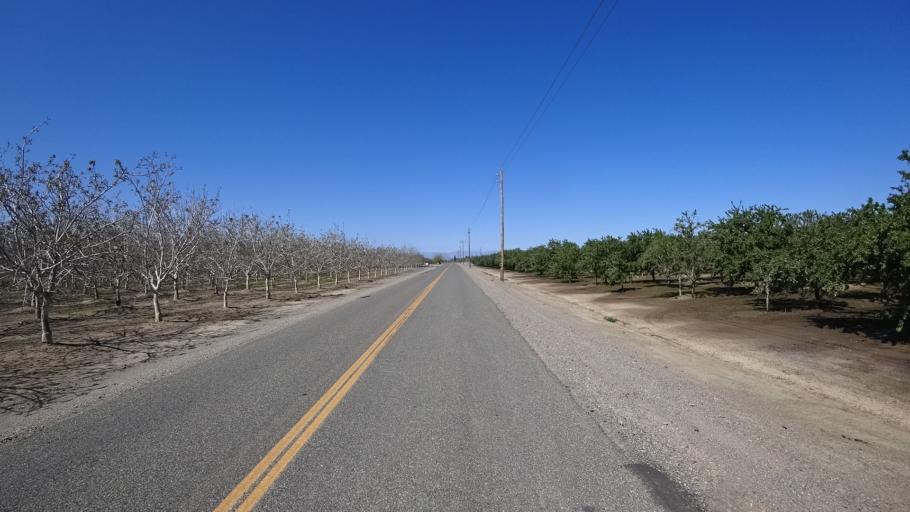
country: US
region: California
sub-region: Glenn County
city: Orland
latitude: 39.7108
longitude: -122.1568
